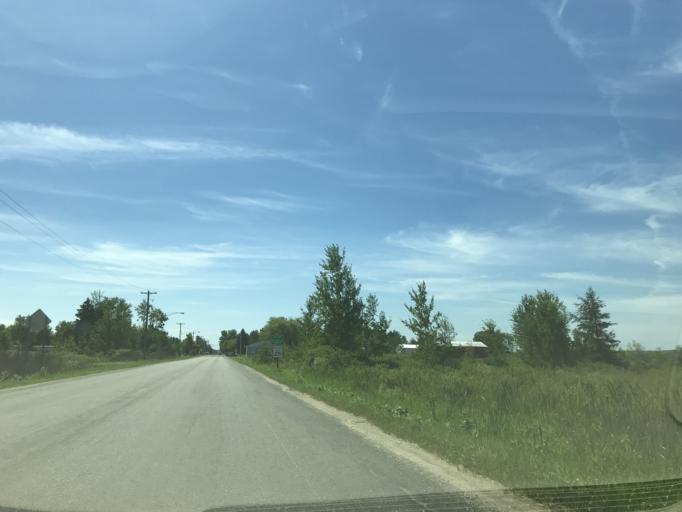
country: US
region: Michigan
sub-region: Roscommon County
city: Houghton Lake
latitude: 44.3351
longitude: -84.9446
